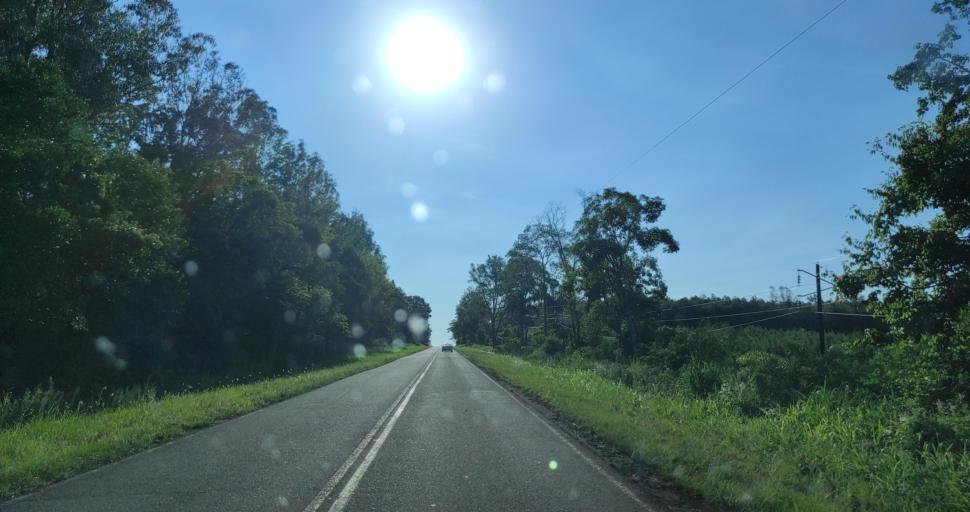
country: AR
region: Misiones
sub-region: Departamento de Eldorado
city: Eldorado
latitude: -26.3995
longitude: -54.3746
